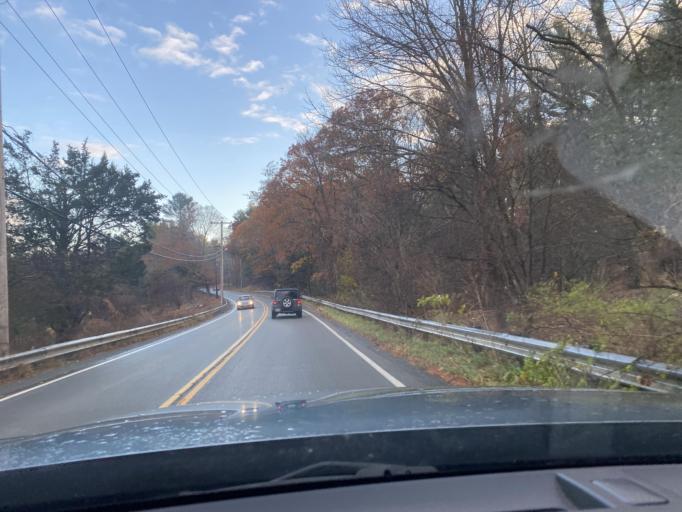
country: US
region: Massachusetts
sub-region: Norfolk County
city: Dover
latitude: 42.2535
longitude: -71.2502
